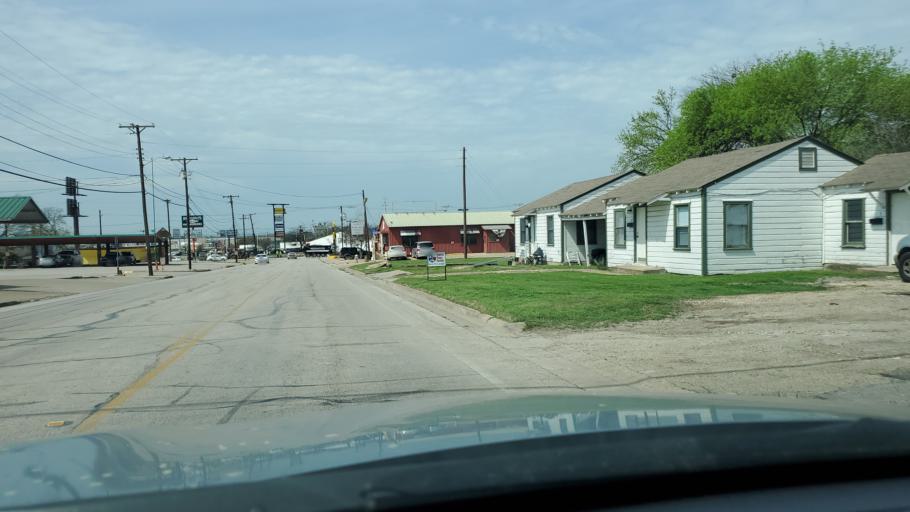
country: US
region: Texas
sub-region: Bell County
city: Temple
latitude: 31.0921
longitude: -97.3745
